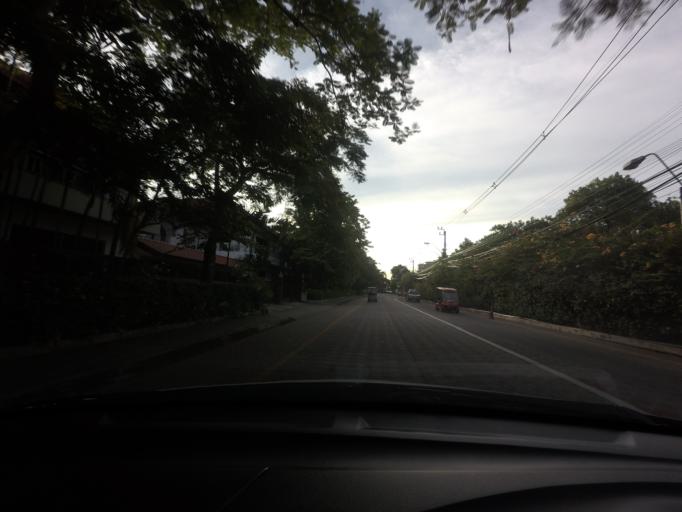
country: TH
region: Nonthaburi
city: Mueang Nonthaburi
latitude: 13.8918
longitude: 100.5263
